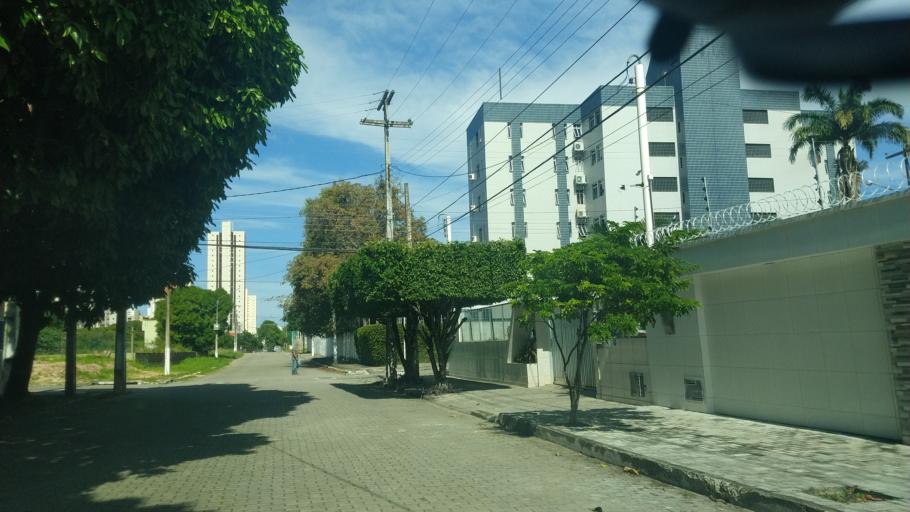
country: BR
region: Rio Grande do Norte
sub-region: Natal
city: Natal
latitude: -5.8605
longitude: -35.1992
